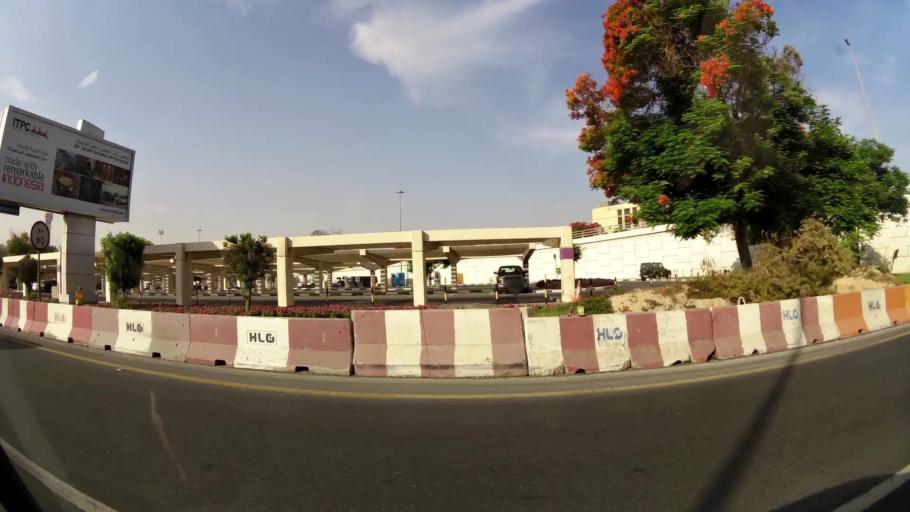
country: AE
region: Ash Shariqah
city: Sharjah
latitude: 25.2488
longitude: 55.3502
